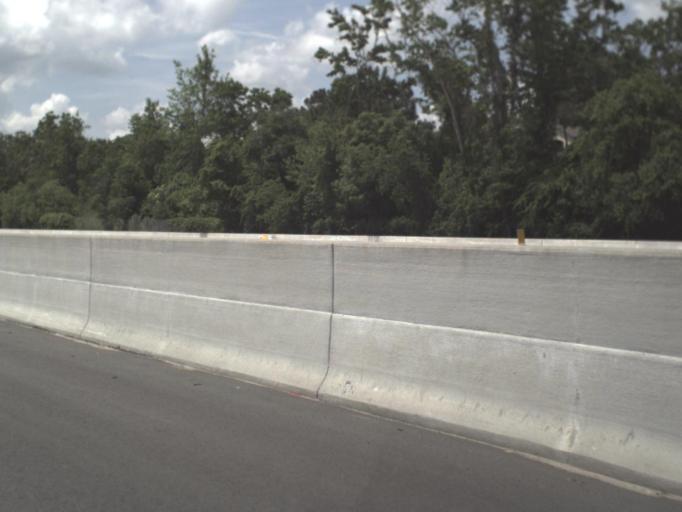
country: US
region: Florida
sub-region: Clay County
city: Bellair-Meadowbrook Terrace
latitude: 30.2013
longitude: -81.7510
